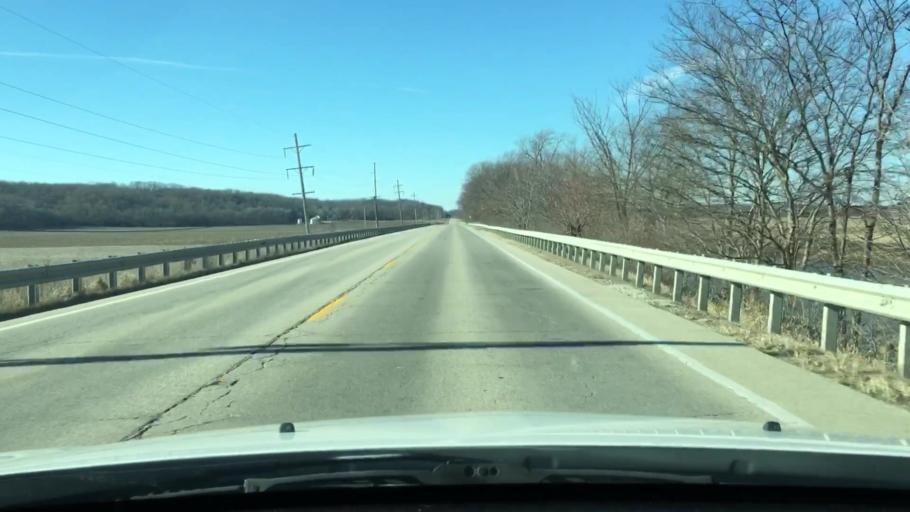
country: US
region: Illinois
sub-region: Mason County
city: Havana
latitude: 40.3022
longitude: -90.1206
